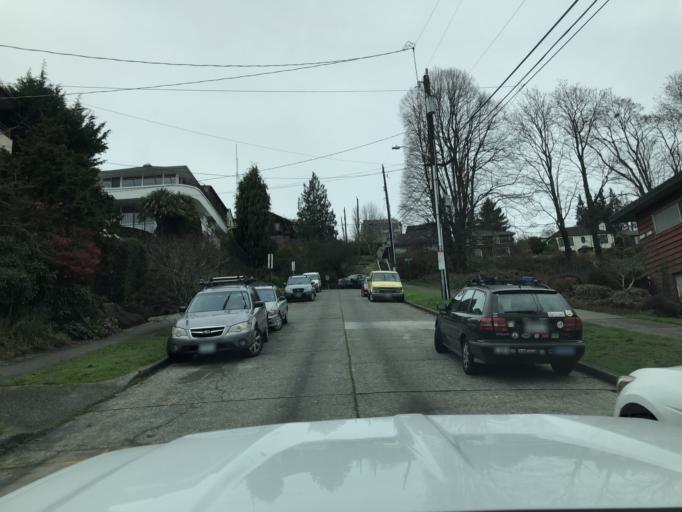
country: US
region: Washington
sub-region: King County
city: Seattle
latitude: 47.6274
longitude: -122.3528
